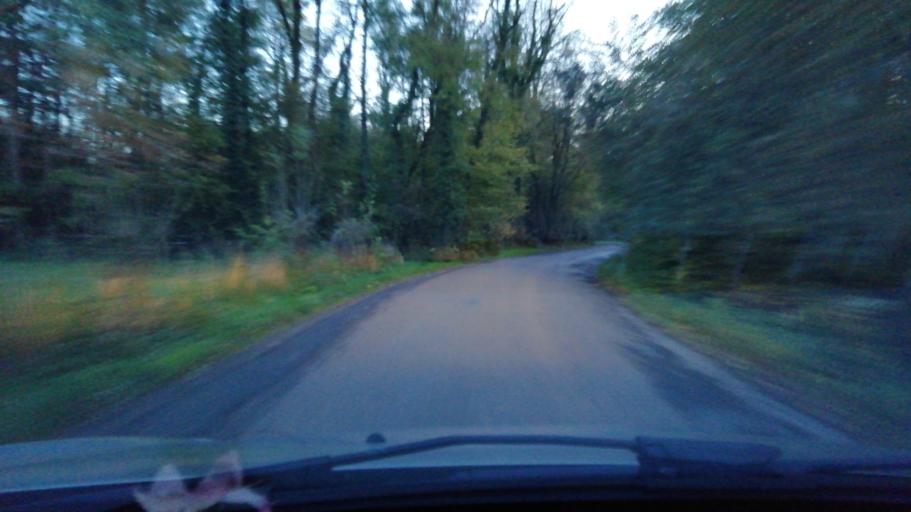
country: FR
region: Nord-Pas-de-Calais
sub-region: Departement du Nord
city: Marpent
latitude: 50.2772
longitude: 4.0890
